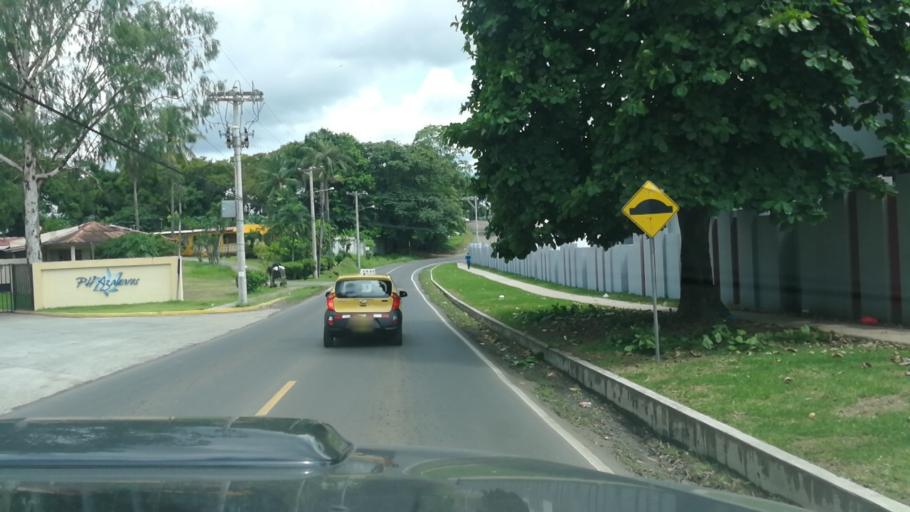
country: PA
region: Panama
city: Tocumen
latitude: 9.0748
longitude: -79.4283
